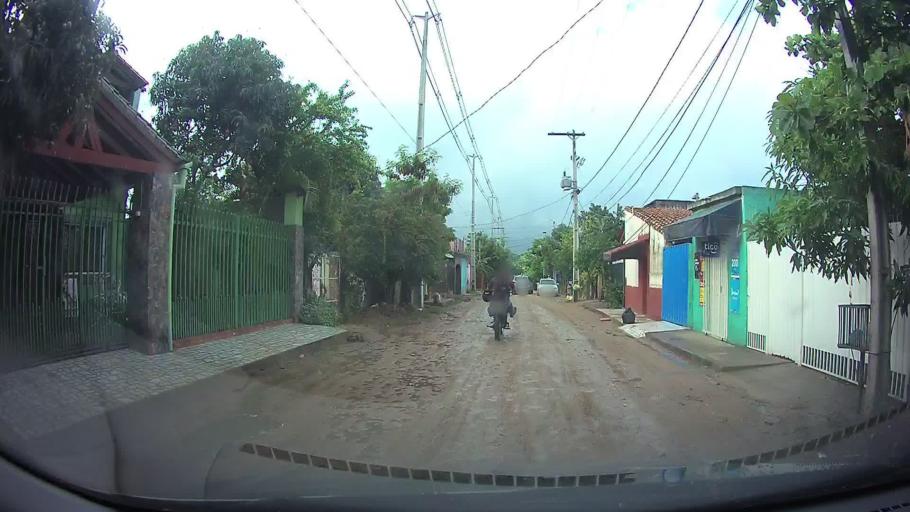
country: PY
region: Asuncion
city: Asuncion
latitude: -25.2477
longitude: -57.5829
